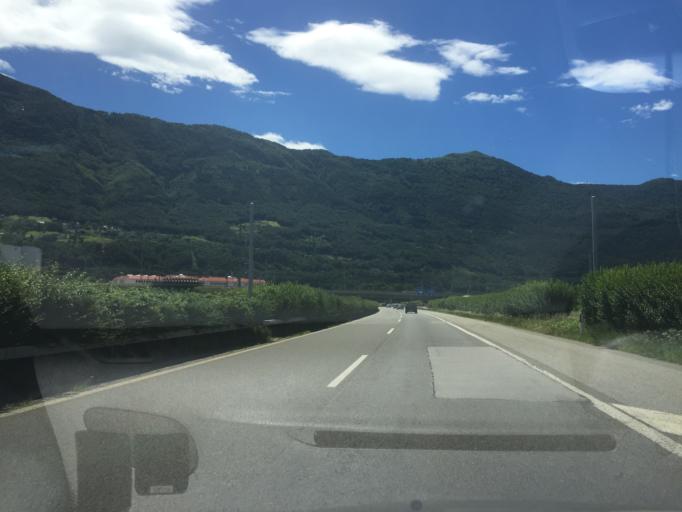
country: CH
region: Ticino
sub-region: Bellinzona District
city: Camorino
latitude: 46.1693
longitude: 8.9908
